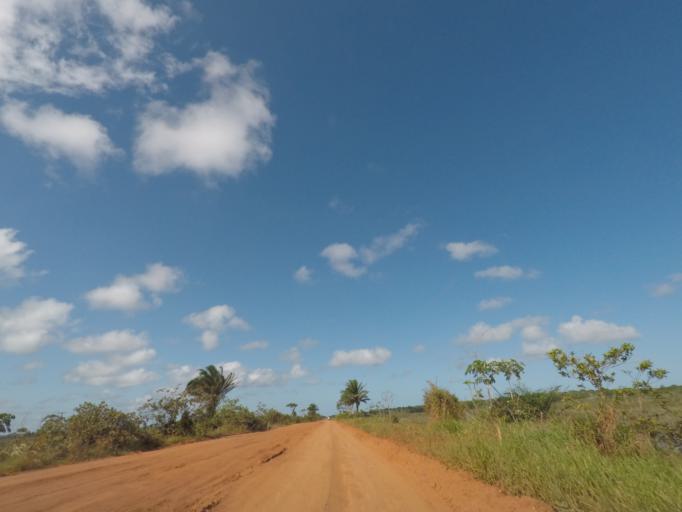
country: BR
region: Bahia
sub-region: Marau
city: Marau
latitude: -14.1718
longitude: -39.0181
